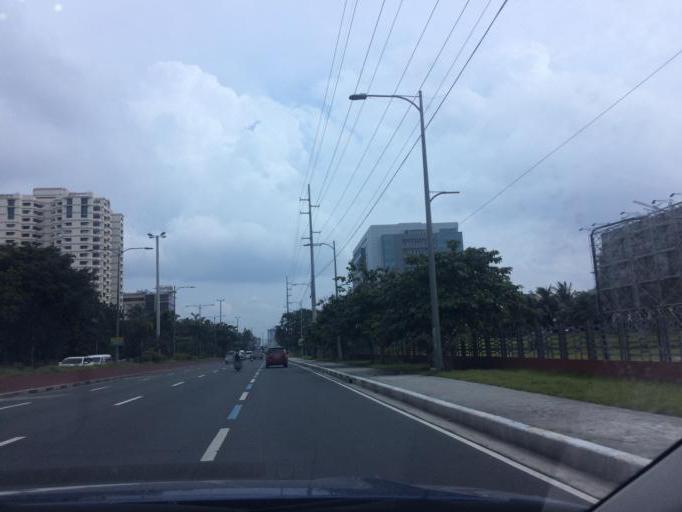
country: PH
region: Metro Manila
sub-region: Makati City
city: Makati City
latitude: 14.5429
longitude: 120.9915
